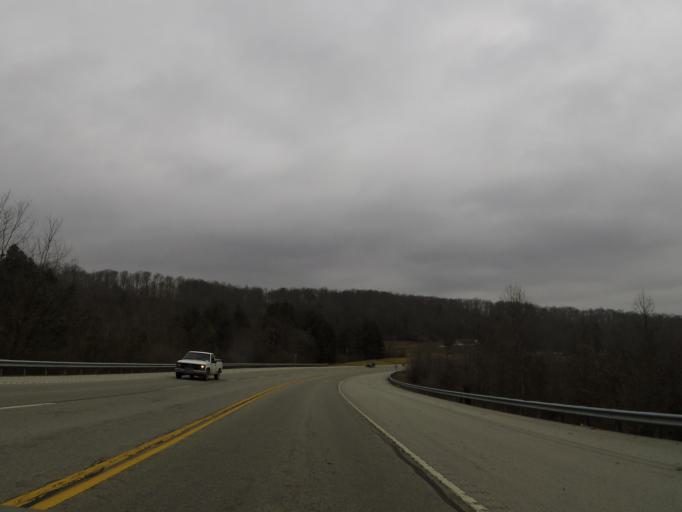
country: US
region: Tennessee
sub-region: Scott County
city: Huntsville
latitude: 36.3802
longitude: -84.5665
